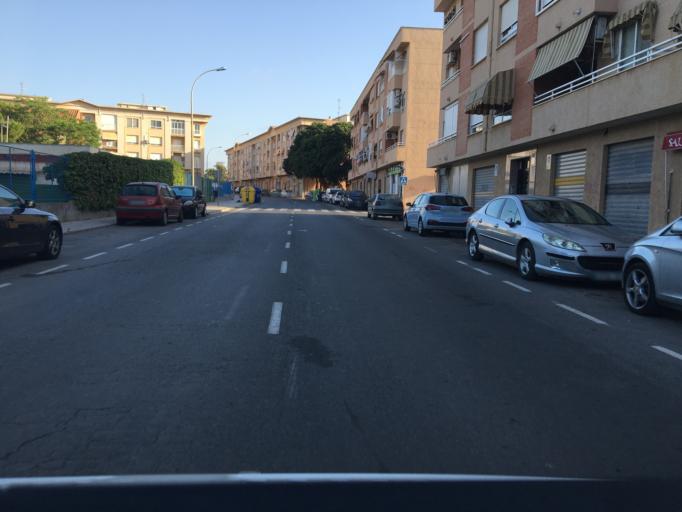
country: ES
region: Murcia
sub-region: Murcia
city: Cartagena
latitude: 37.6222
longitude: -1.0064
